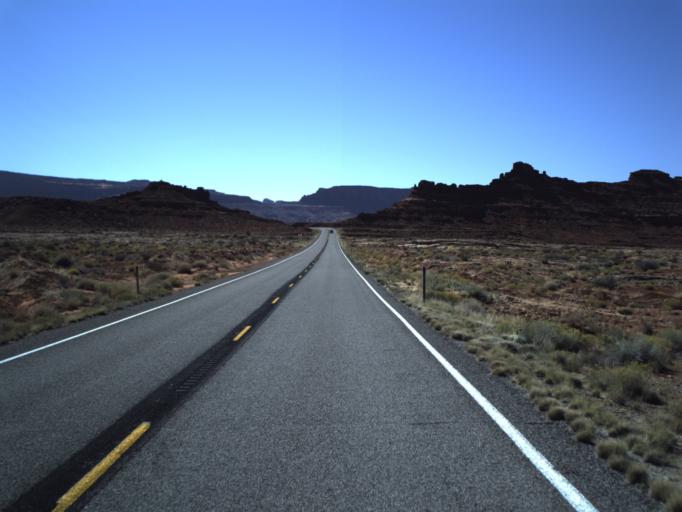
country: US
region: Utah
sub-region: San Juan County
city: Blanding
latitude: 37.8326
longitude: -110.3577
